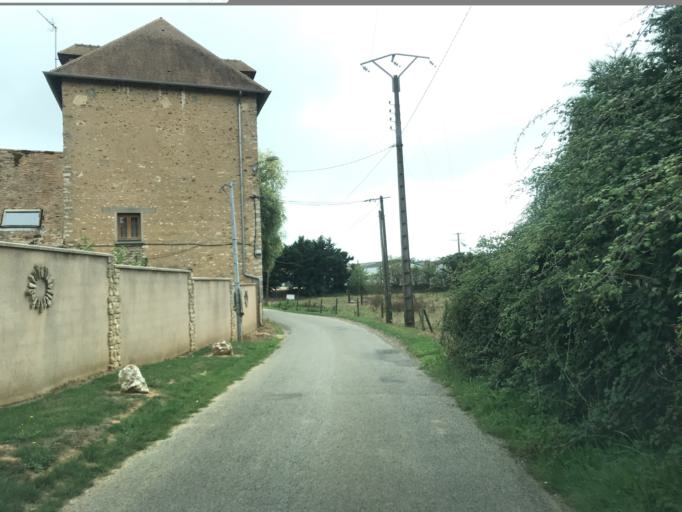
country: FR
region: Haute-Normandie
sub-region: Departement de l'Eure
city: Houlbec-Cocherel
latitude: 49.0541
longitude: 1.3527
